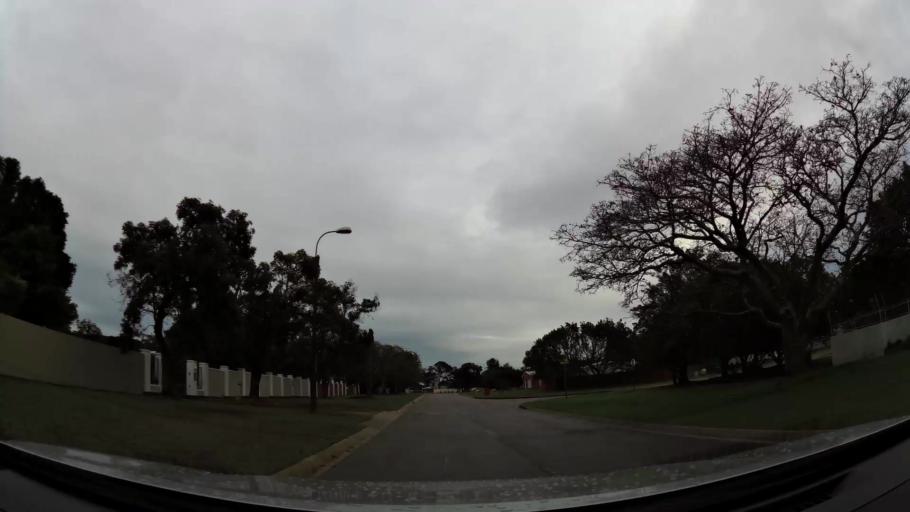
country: ZA
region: Eastern Cape
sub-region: Nelson Mandela Bay Metropolitan Municipality
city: Port Elizabeth
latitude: -33.9776
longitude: 25.5661
